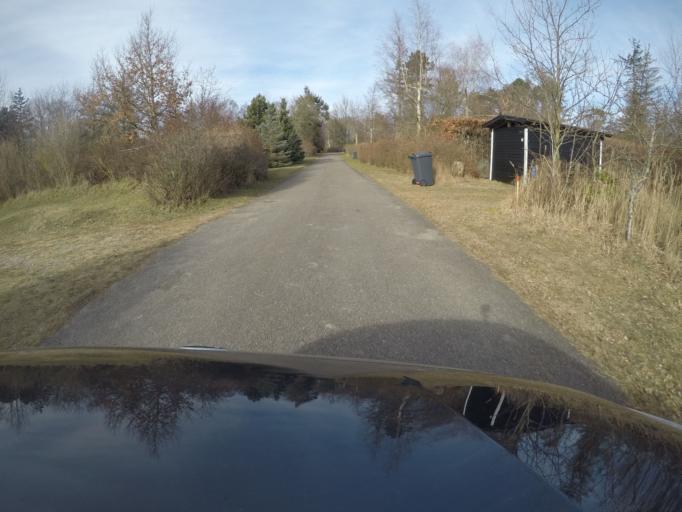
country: DK
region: Capital Region
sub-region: Halsnaes Kommune
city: Liseleje
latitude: 55.9945
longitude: 11.9252
